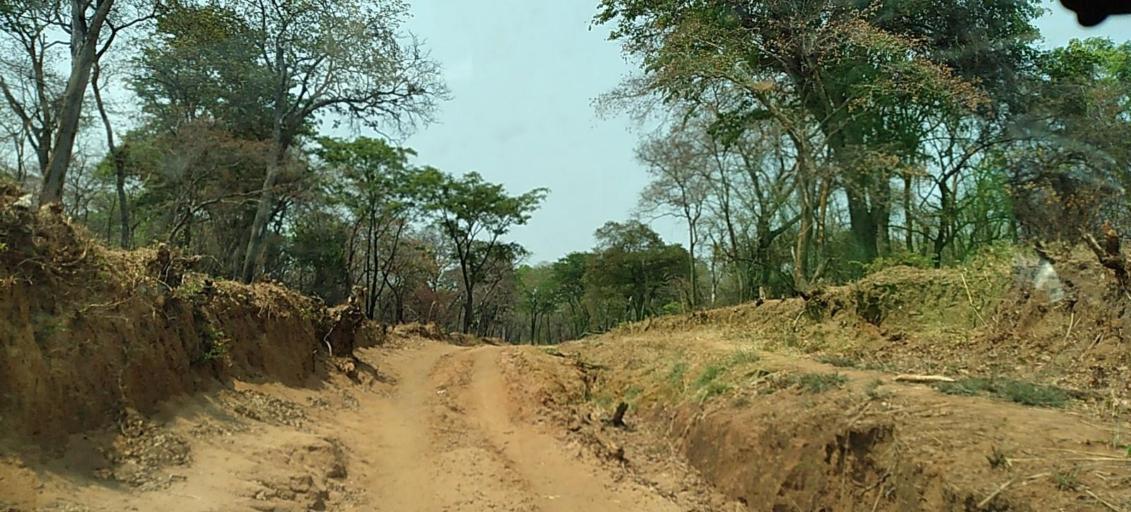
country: ZM
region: Western
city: Lukulu
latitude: -13.9847
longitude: 23.2285
